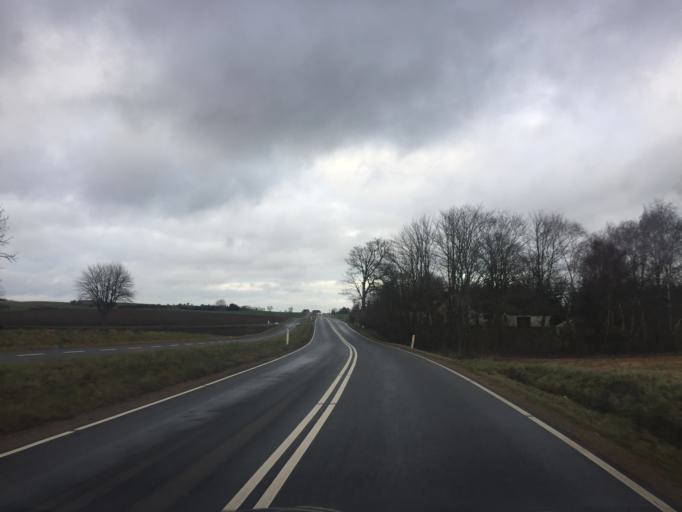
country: DK
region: Zealand
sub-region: Holbaek Kommune
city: Tollose
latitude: 55.5989
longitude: 11.6972
